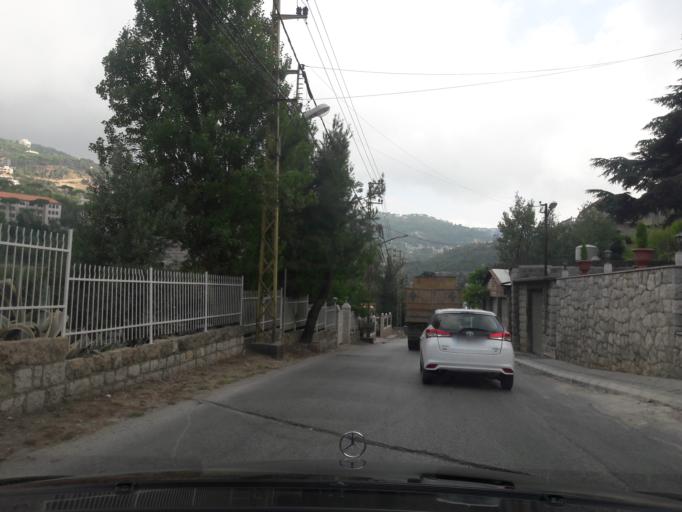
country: LB
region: Mont-Liban
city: Djounie
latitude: 33.9268
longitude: 35.7315
